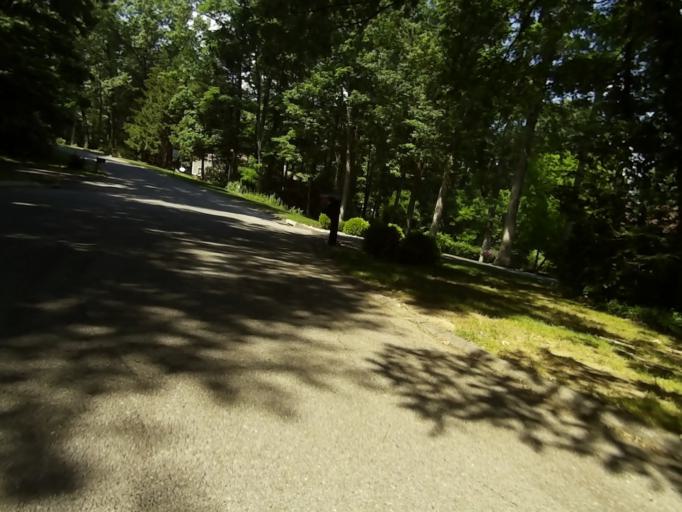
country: US
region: Pennsylvania
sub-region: Centre County
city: Park Forest Village
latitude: 40.7930
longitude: -77.9122
